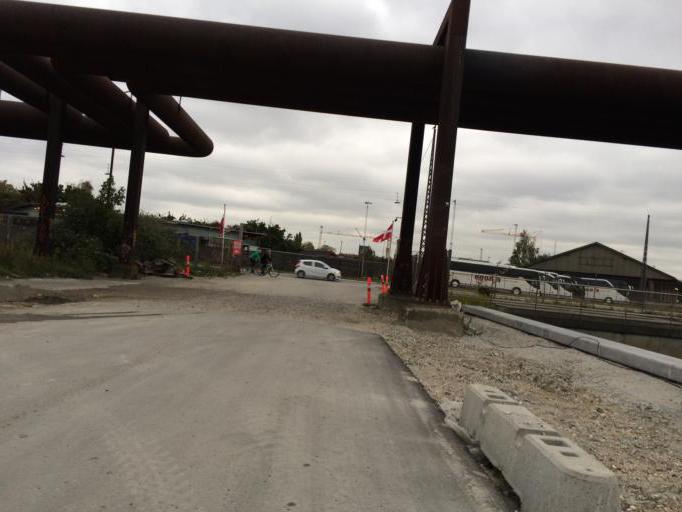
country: DK
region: Capital Region
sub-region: Kobenhavn
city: Copenhagen
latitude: 55.6566
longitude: 12.5527
